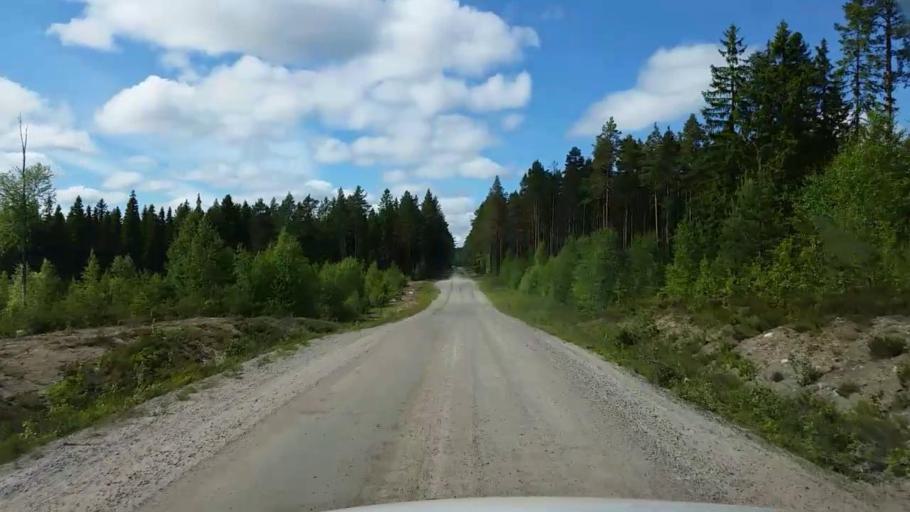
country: SE
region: Gaevleborg
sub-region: Ovanakers Kommun
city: Edsbyn
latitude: 61.5738
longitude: 15.9151
